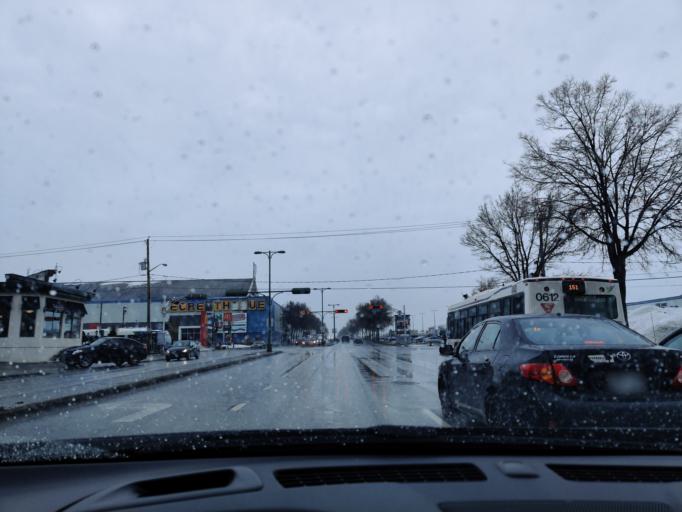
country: CA
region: Quebec
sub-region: Laval
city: Laval
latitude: 45.5406
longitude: -73.7480
